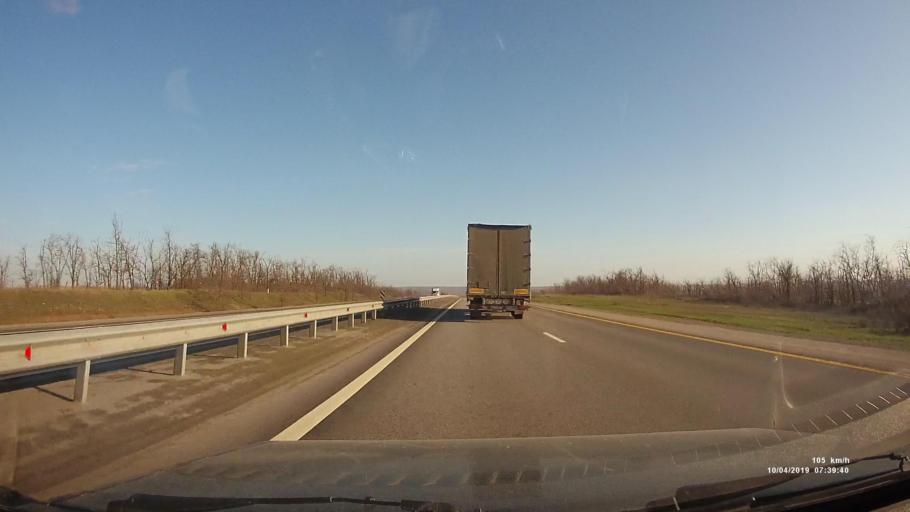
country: RU
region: Rostov
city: Likhoy
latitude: 48.1078
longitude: 40.2600
